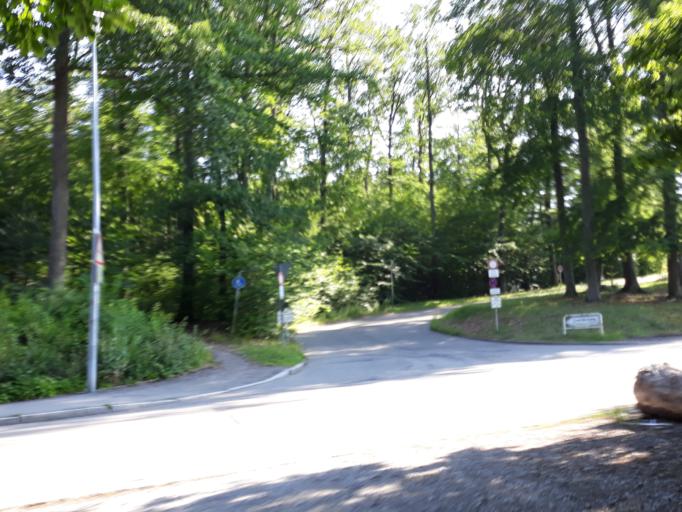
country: DE
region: Baden-Wuerttemberg
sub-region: Regierungsbezirk Stuttgart
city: Sindelfingen
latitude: 48.6909
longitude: 9.0361
